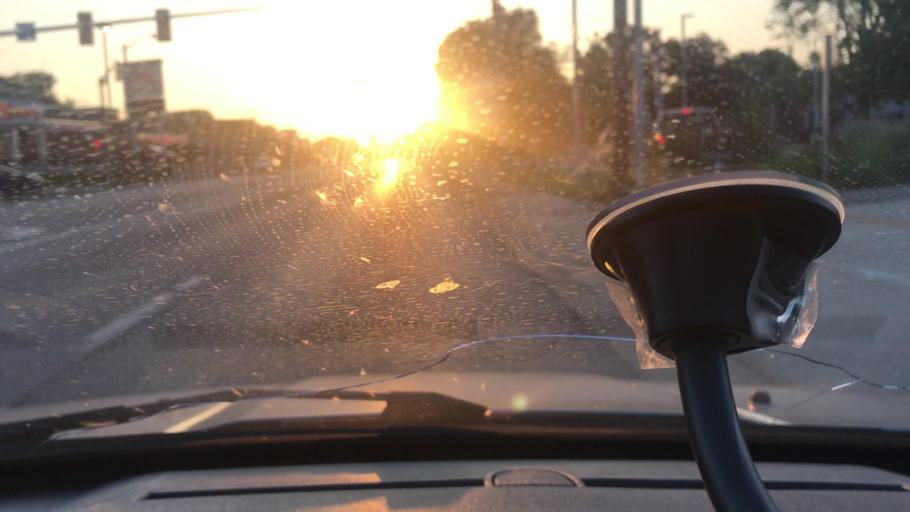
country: US
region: Illinois
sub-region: Tazewell County
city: Pekin
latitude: 40.5652
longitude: -89.6362
